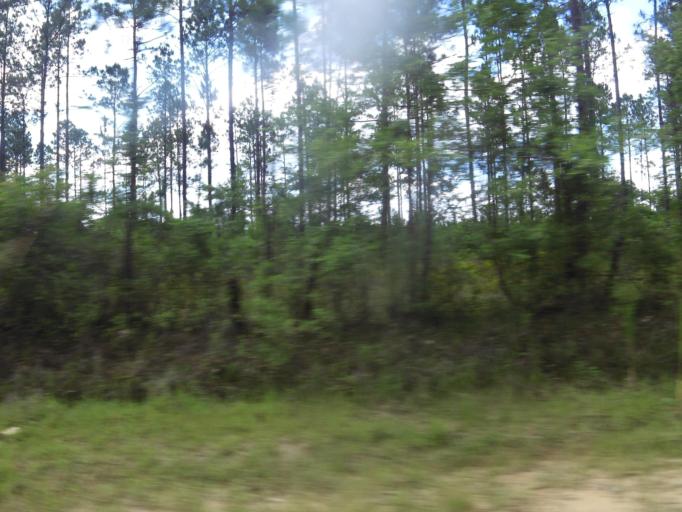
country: US
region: Florida
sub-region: Clay County
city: Asbury Lake
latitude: 29.8956
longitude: -81.8629
